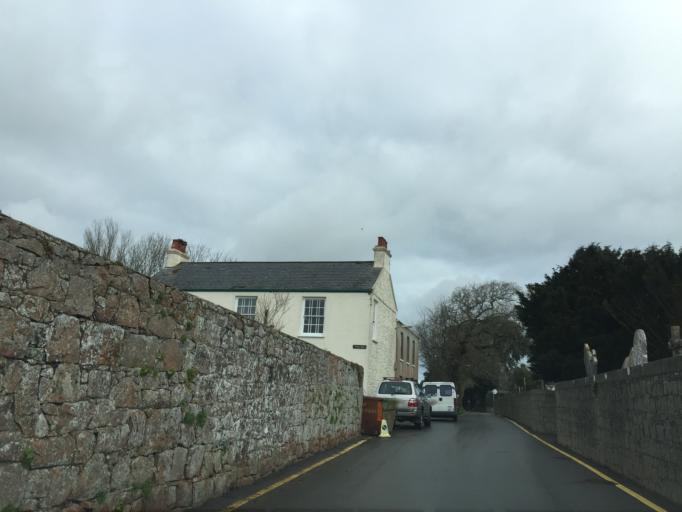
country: JE
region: St Helier
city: Saint Helier
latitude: 49.2143
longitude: -2.1422
